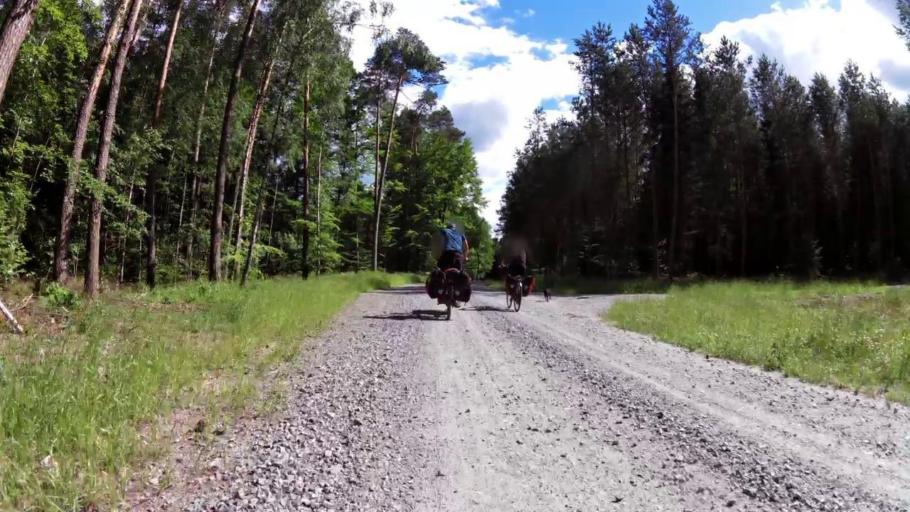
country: PL
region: West Pomeranian Voivodeship
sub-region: Powiat lobeski
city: Lobez
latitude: 53.6816
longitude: 15.5507
